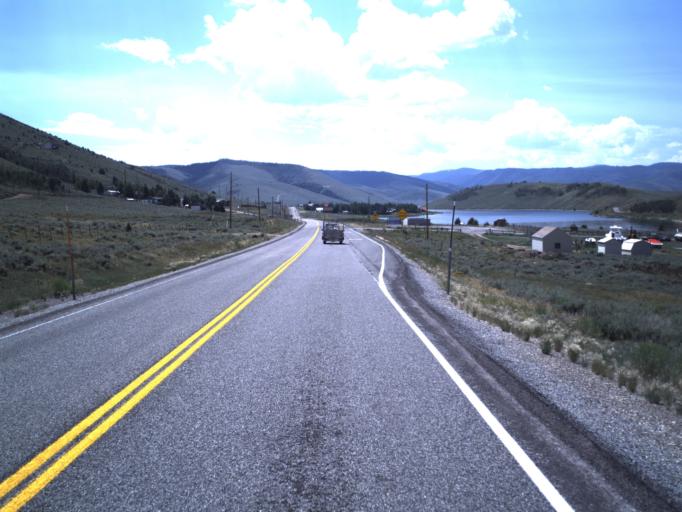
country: US
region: Utah
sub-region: Carbon County
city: Helper
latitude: 39.8179
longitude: -111.1354
